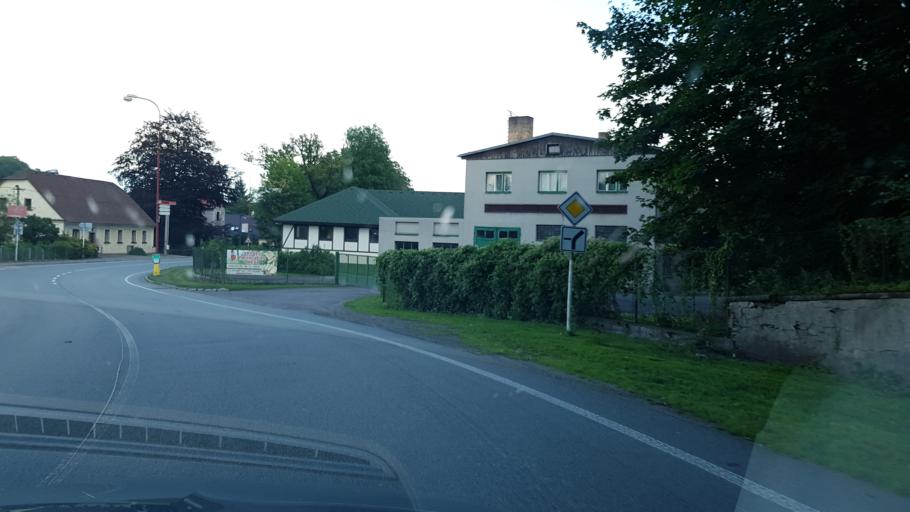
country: CZ
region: Pardubicky
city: Zamberk
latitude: 50.0857
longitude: 16.4684
